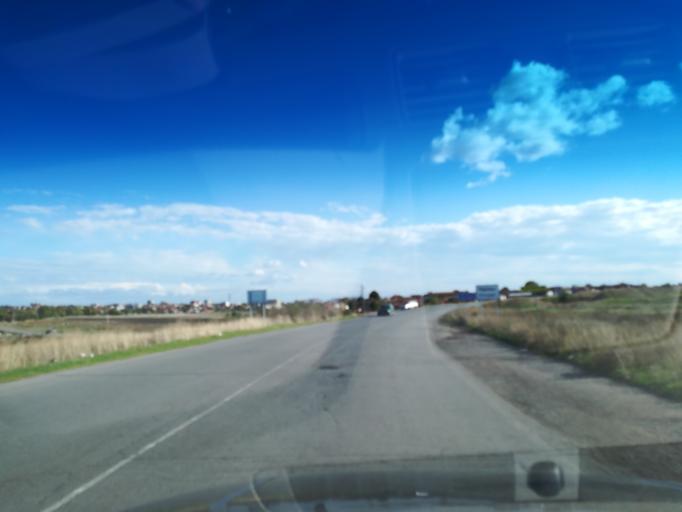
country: BG
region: Stara Zagora
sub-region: Obshtina Chirpan
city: Chirpan
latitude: 42.2059
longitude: 25.3077
